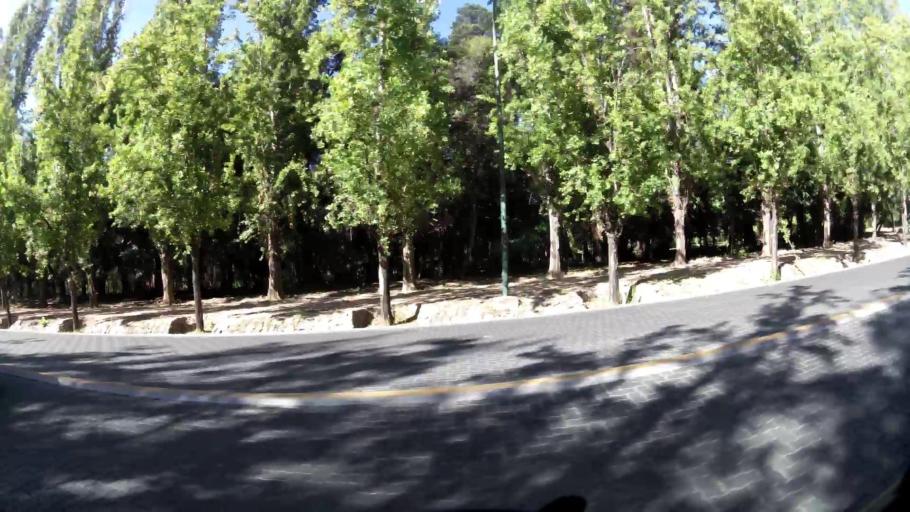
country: AR
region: Mendoza
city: Mendoza
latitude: -32.8851
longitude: -68.8696
